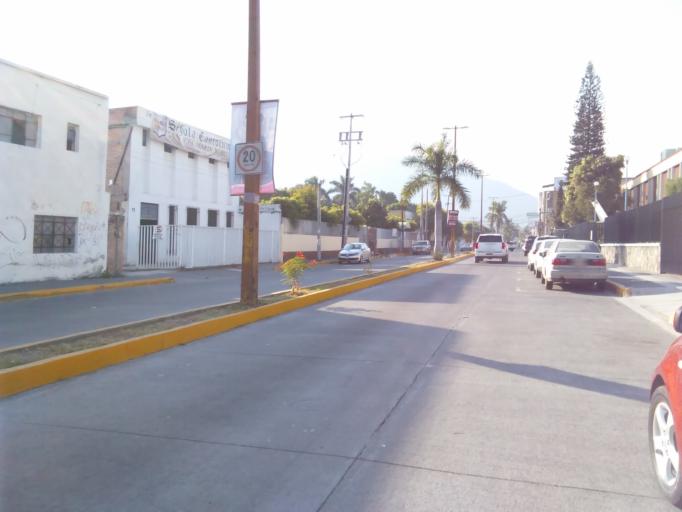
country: MX
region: Nayarit
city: Tepic
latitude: 21.4992
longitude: -104.8979
